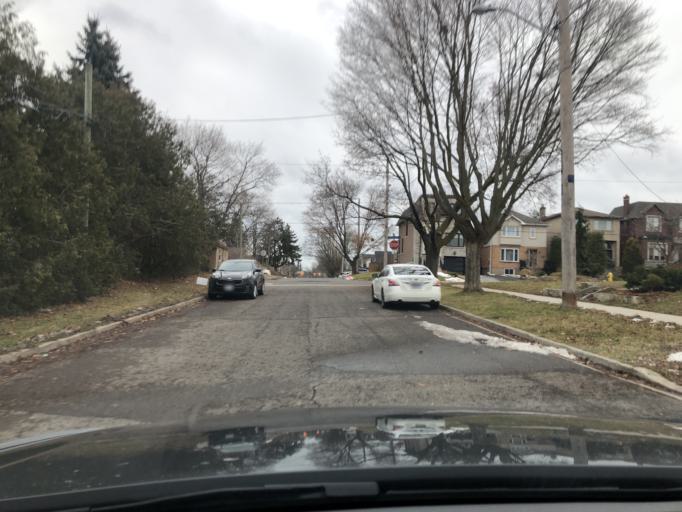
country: CA
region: Ontario
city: Etobicoke
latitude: 43.6993
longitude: -79.5285
